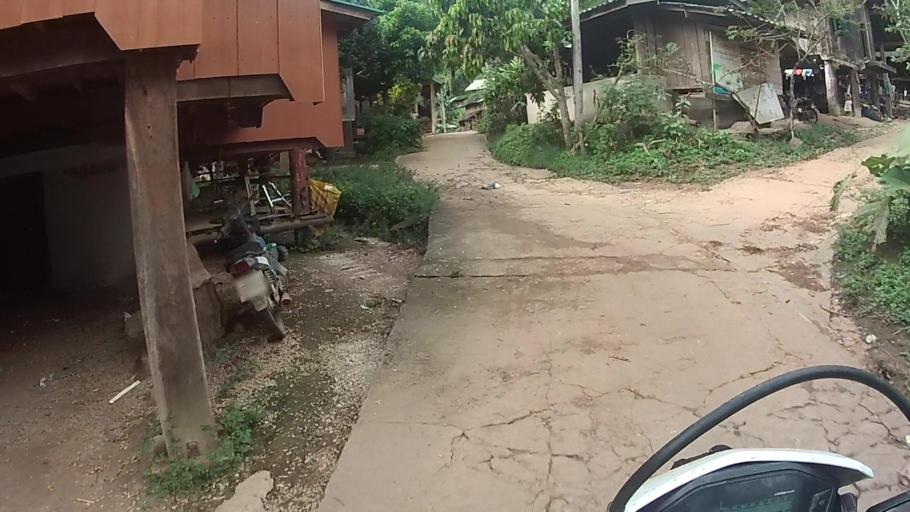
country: TH
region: Lampang
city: Wang Nuea
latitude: 19.0607
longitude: 99.5037
